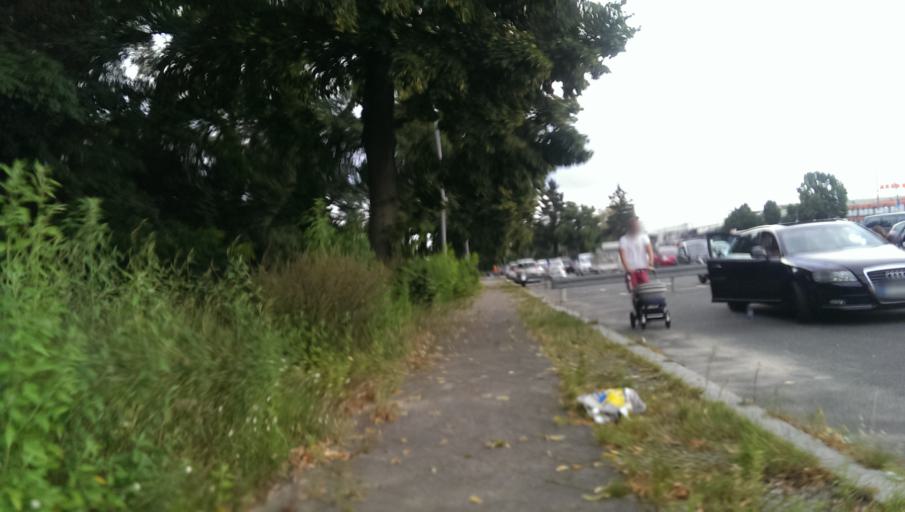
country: DE
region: Berlin
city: Lichterfelde
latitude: 52.4197
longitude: 13.2892
